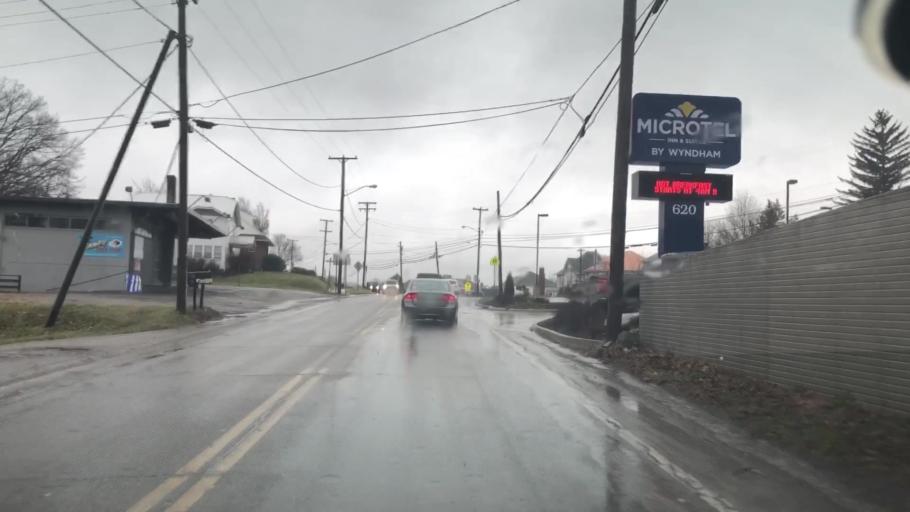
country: US
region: Ohio
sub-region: Harrison County
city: Cadiz
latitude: 40.2802
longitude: -81.0005
